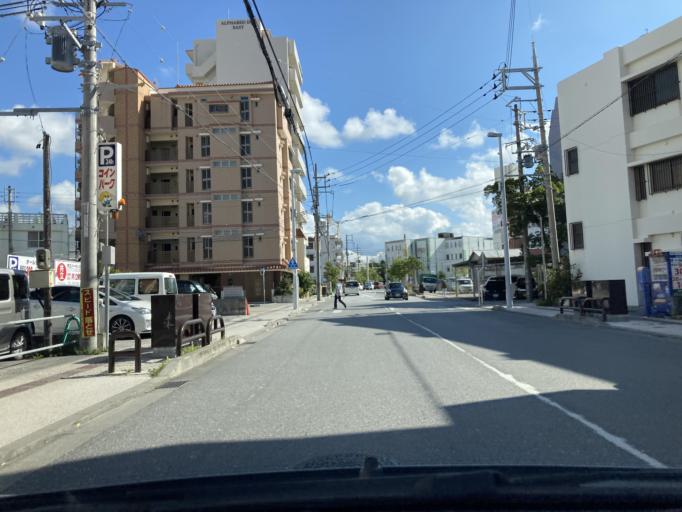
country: JP
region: Okinawa
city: Naha-shi
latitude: 26.2129
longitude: 127.6905
